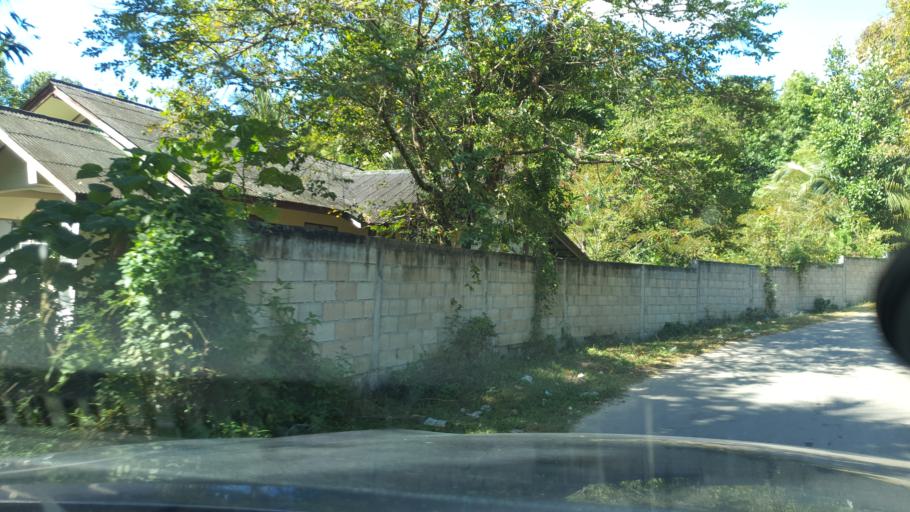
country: TH
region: Phangnga
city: Ban Ao Nang
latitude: 8.0296
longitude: 98.8602
